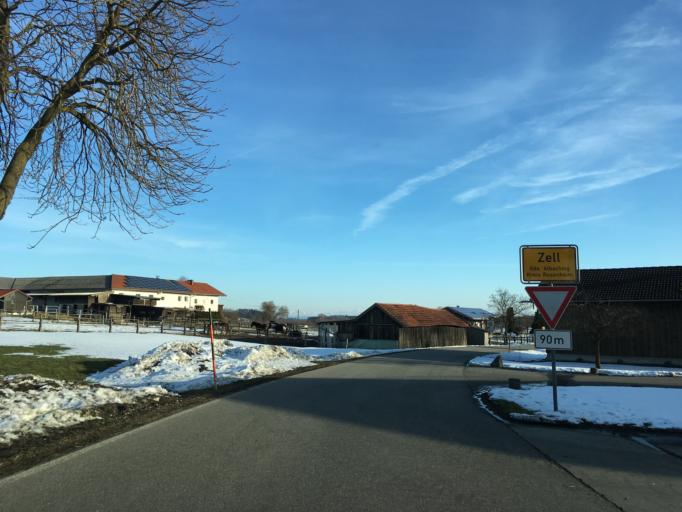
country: DE
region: Bavaria
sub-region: Upper Bavaria
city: Albaching
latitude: 48.1006
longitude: 12.0966
